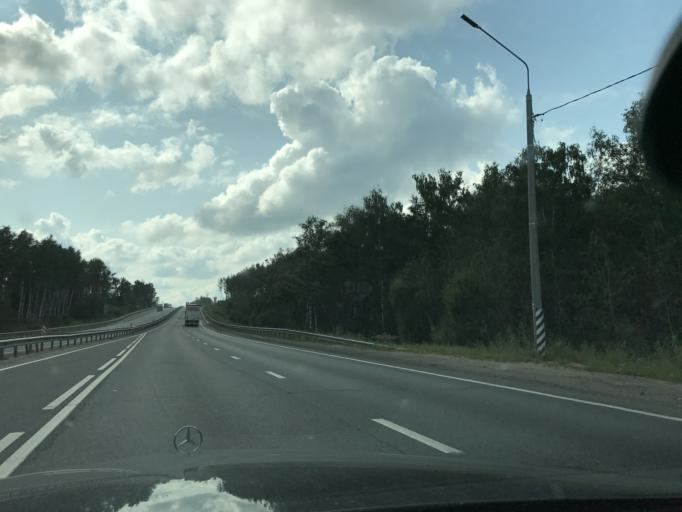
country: RU
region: Vladimir
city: Gorokhovets
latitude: 56.1827
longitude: 42.6673
